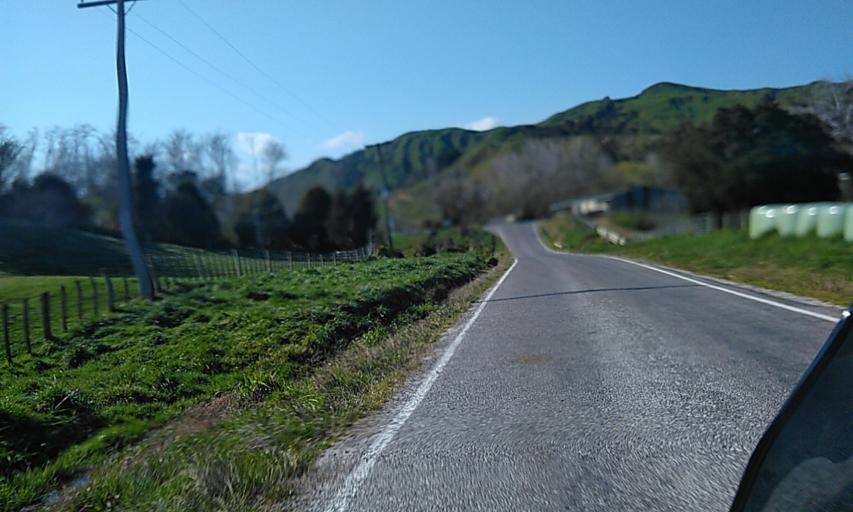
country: NZ
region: Gisborne
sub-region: Gisborne District
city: Gisborne
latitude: -38.5035
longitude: 178.0550
